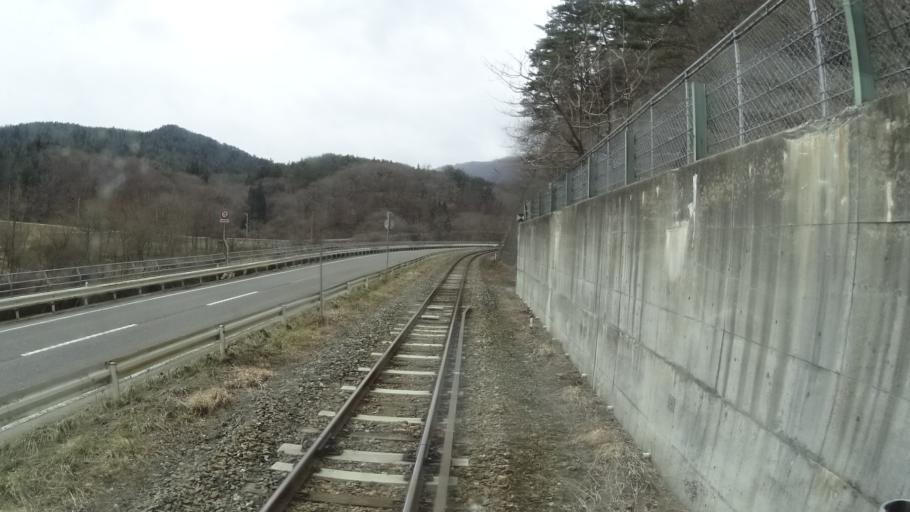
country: JP
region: Iwate
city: Tono
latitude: 39.3030
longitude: 141.3885
